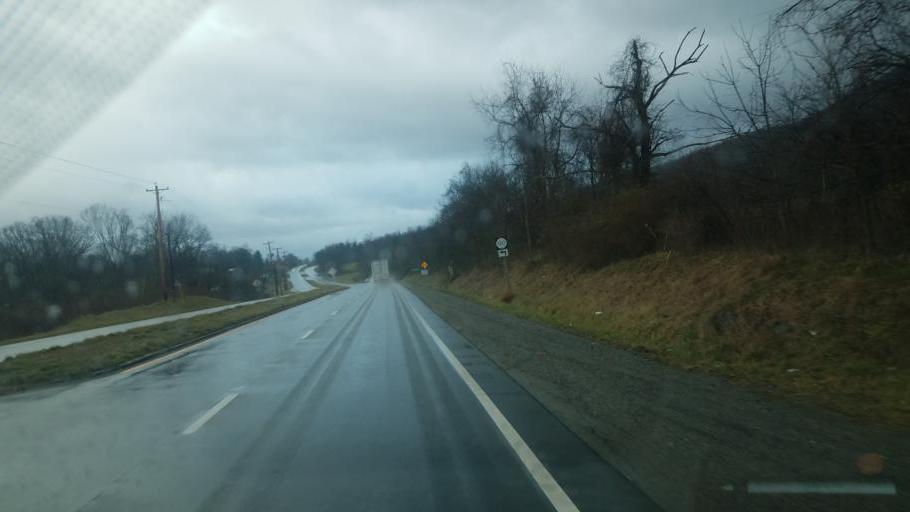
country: US
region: Virginia
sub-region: Giles County
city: Pearisburg
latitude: 37.3187
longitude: -80.7309
